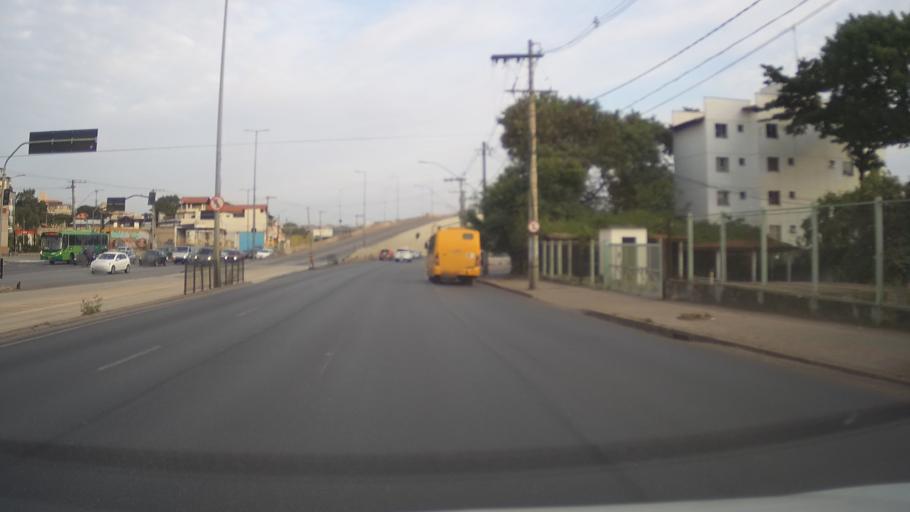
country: BR
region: Minas Gerais
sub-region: Belo Horizonte
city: Belo Horizonte
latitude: -19.8705
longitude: -43.9277
